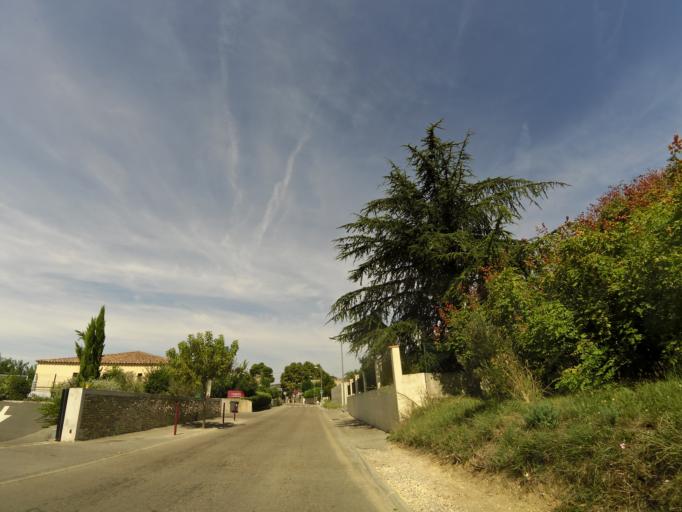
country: FR
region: Languedoc-Roussillon
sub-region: Departement du Gard
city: Calvisson
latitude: 43.7838
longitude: 4.1962
